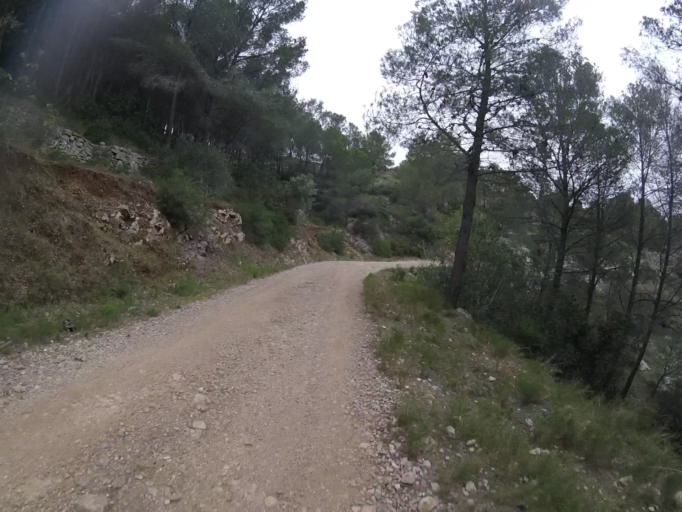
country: ES
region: Valencia
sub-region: Provincia de Castello
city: Alcala de Xivert
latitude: 40.3114
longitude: 0.2637
